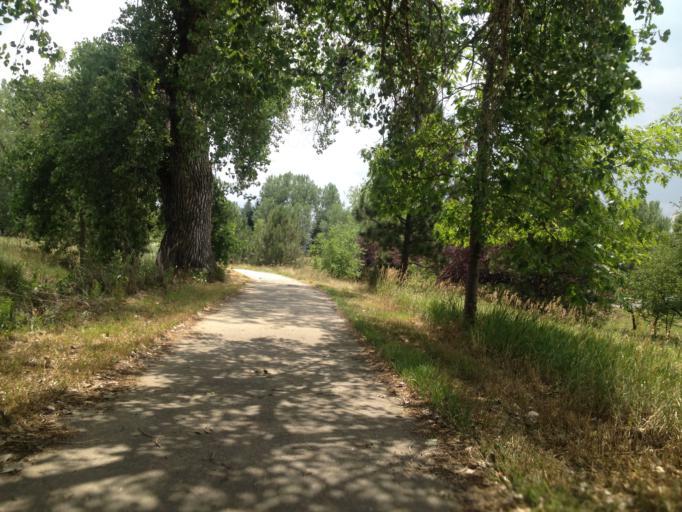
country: US
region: Colorado
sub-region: Boulder County
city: Louisville
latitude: 39.9664
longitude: -105.1499
